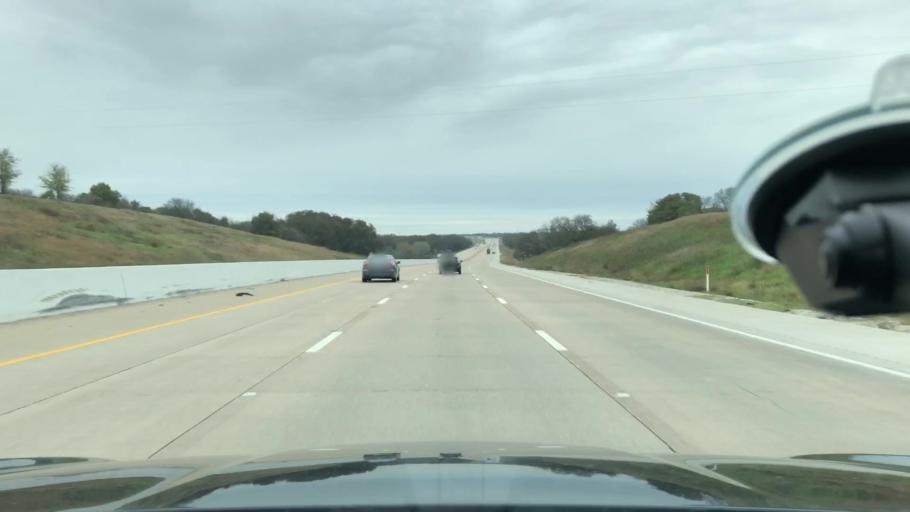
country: US
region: Texas
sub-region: Ellis County
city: Italy
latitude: 32.2206
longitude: -96.8875
